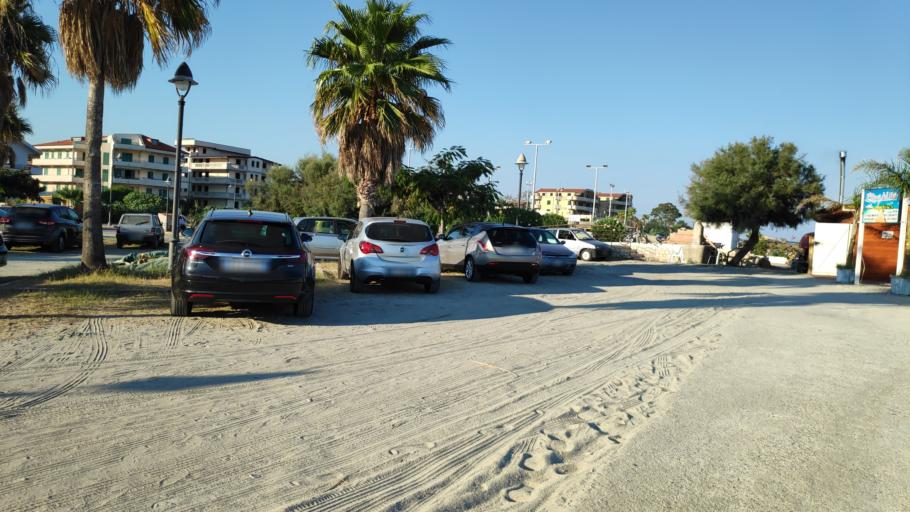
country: IT
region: Calabria
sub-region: Provincia di Reggio Calabria
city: Caulonia Marina
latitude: 38.3411
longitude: 16.4672
